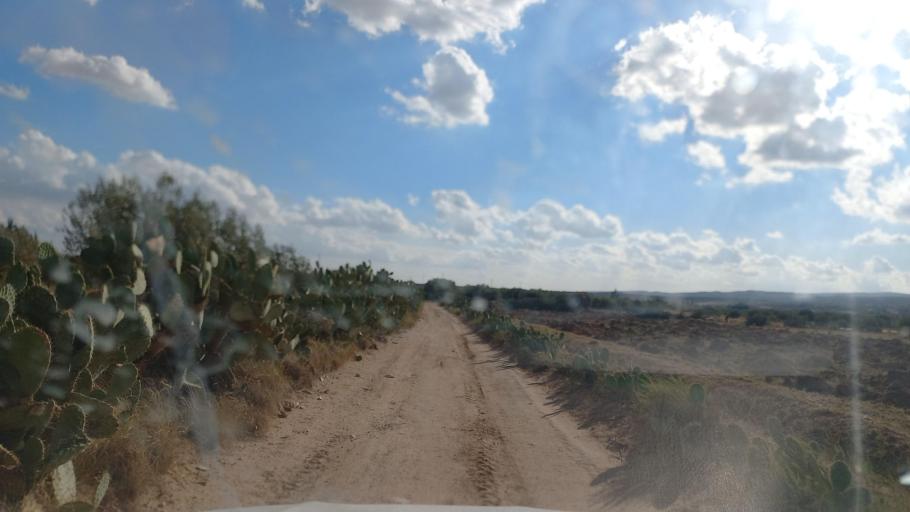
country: TN
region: Al Qasrayn
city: Sbiba
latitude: 35.3852
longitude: 9.0384
